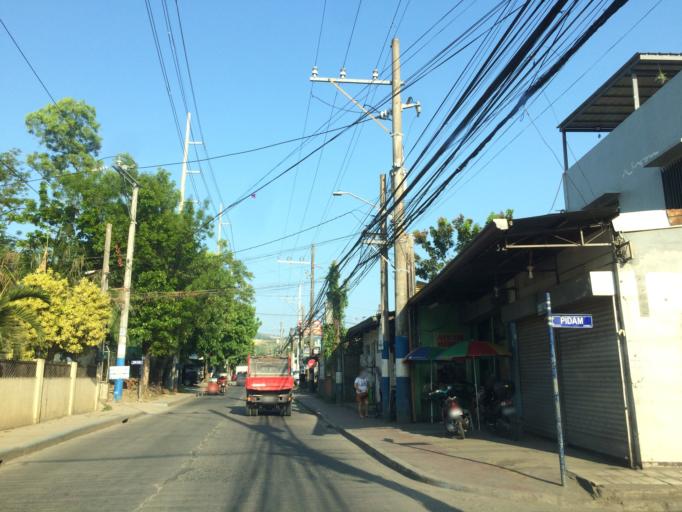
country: PH
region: Calabarzon
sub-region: Province of Rizal
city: San Mateo
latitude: 14.6807
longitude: 121.1204
